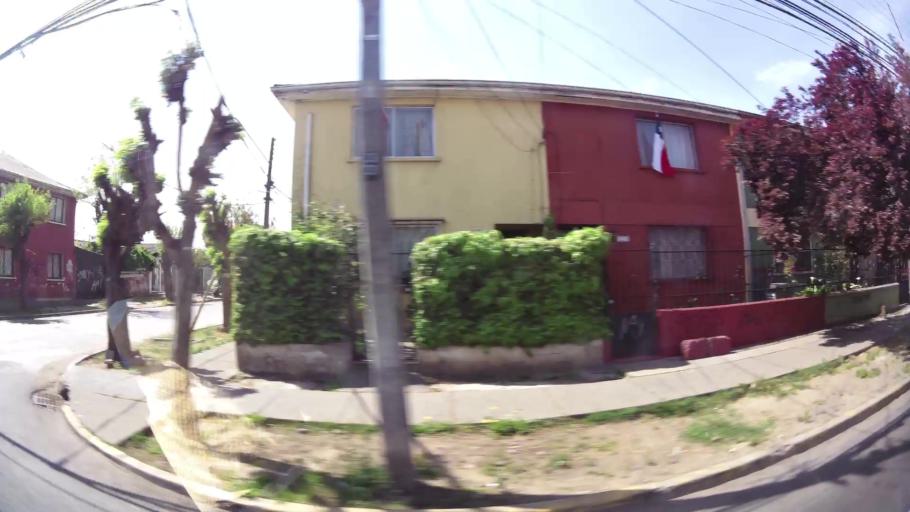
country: CL
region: Santiago Metropolitan
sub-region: Provincia de Santiago
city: Lo Prado
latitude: -33.4194
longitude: -70.7030
